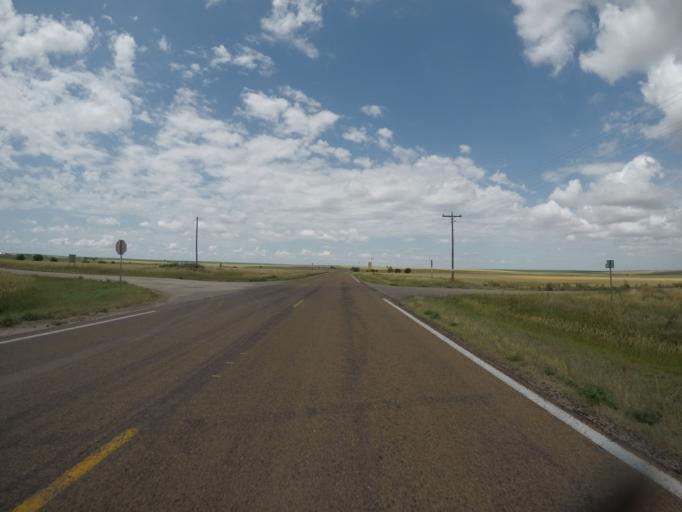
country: US
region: Kansas
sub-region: Rawlins County
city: Atwood
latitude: 39.9435
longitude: -101.0560
